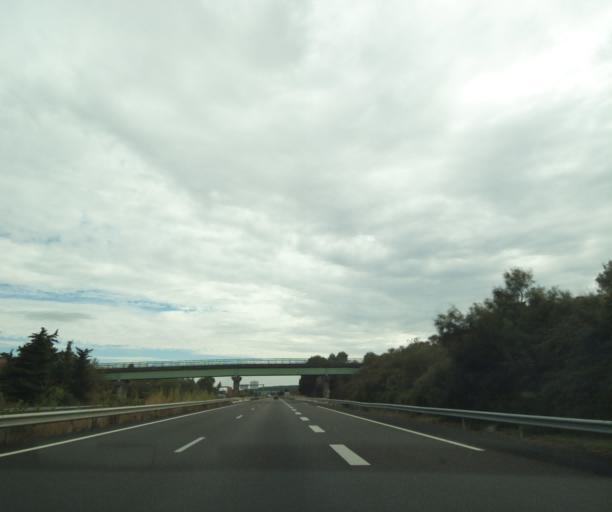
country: FR
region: Languedoc-Roussillon
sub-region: Departement du Gard
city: Garons
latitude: 43.7575
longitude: 4.4274
